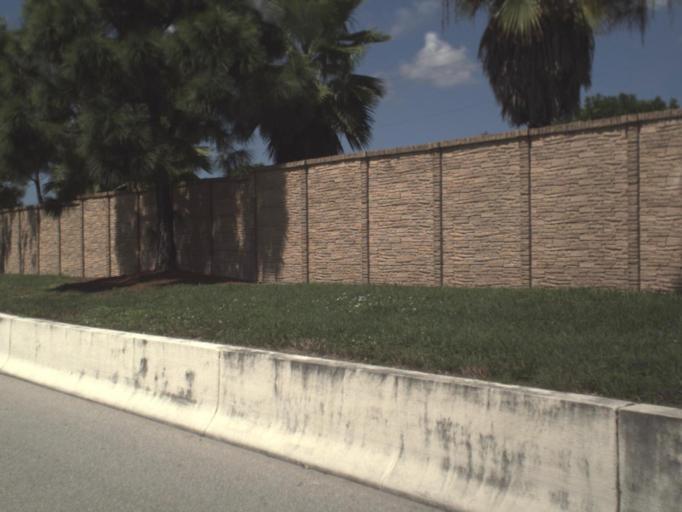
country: US
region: Florida
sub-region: Lee County
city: Cape Coral
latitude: 26.6075
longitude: -81.9473
